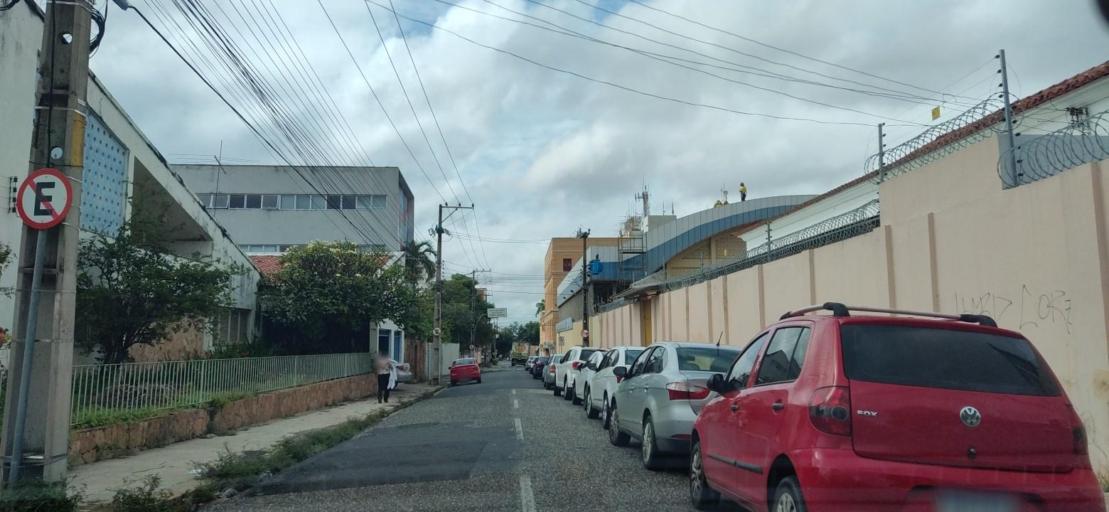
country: BR
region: Piaui
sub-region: Teresina
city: Teresina
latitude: -5.0875
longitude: -42.8095
